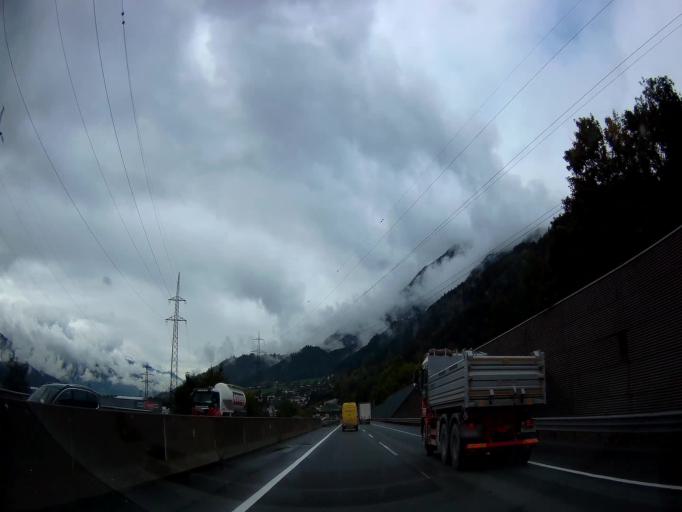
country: AT
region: Tyrol
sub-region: Politischer Bezirk Schwaz
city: Stans
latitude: 47.3627
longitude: 11.7122
